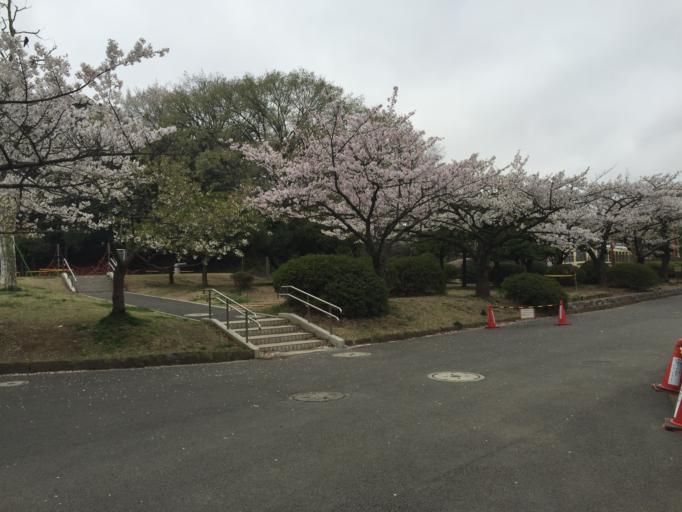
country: JP
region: Kanagawa
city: Yokohama
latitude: 35.4055
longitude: 139.6082
